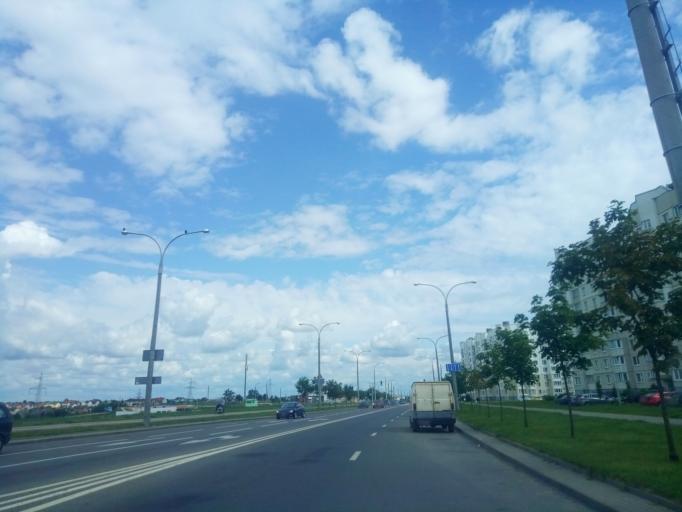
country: BY
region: Minsk
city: Zhdanovichy
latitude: 53.9139
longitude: 27.4147
